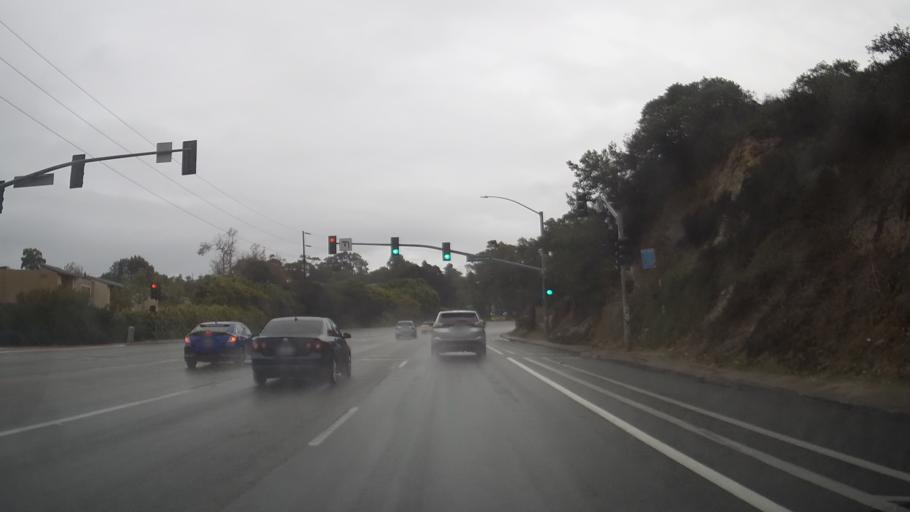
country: US
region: California
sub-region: San Diego County
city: Encinitas
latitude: 33.0487
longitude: -117.2763
